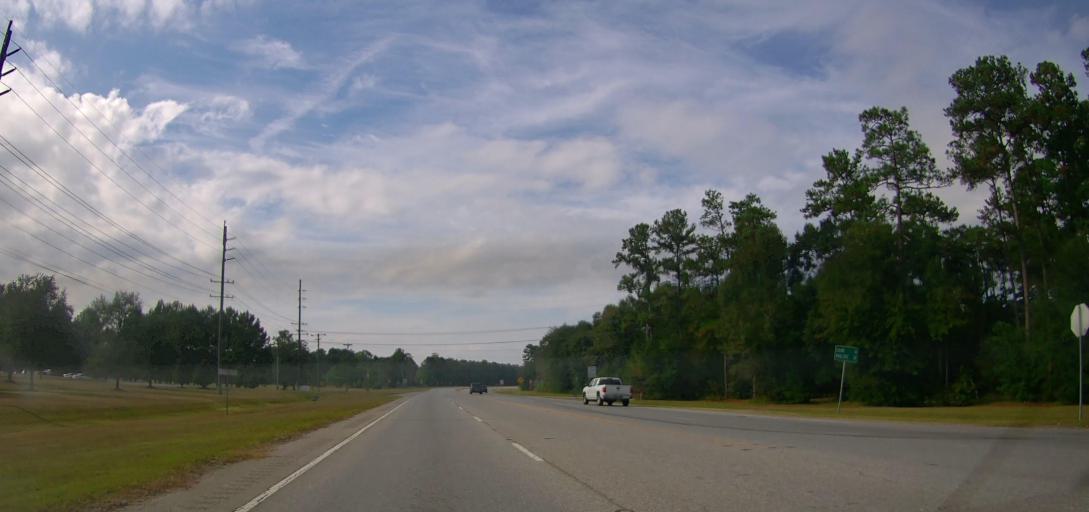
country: US
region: Georgia
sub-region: Thomas County
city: Thomasville
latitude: 30.8180
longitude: -84.0017
